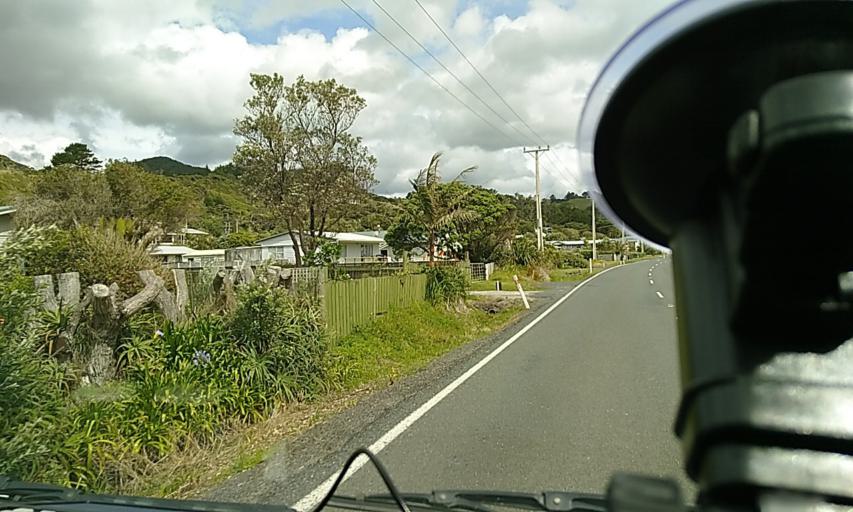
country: NZ
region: Northland
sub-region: Far North District
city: Ahipara
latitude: -35.5203
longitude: 173.3880
